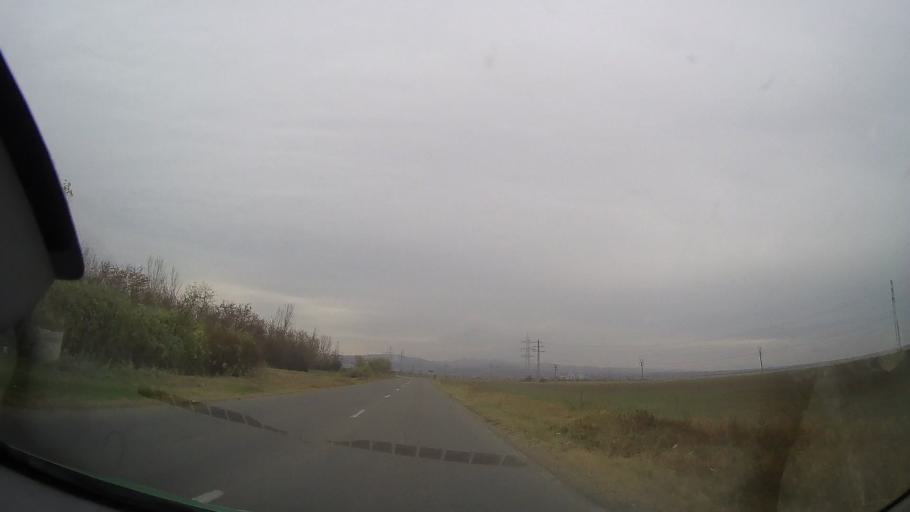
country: RO
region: Prahova
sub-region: Oras Urlati
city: Urlati
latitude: 44.9636
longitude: 26.2340
